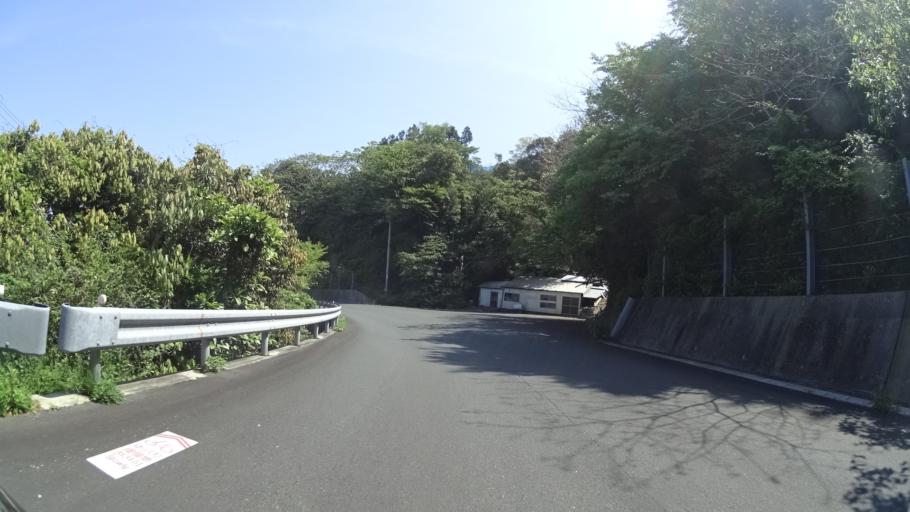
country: JP
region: Oita
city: Tsukumiura
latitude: 33.3638
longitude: 132.0395
